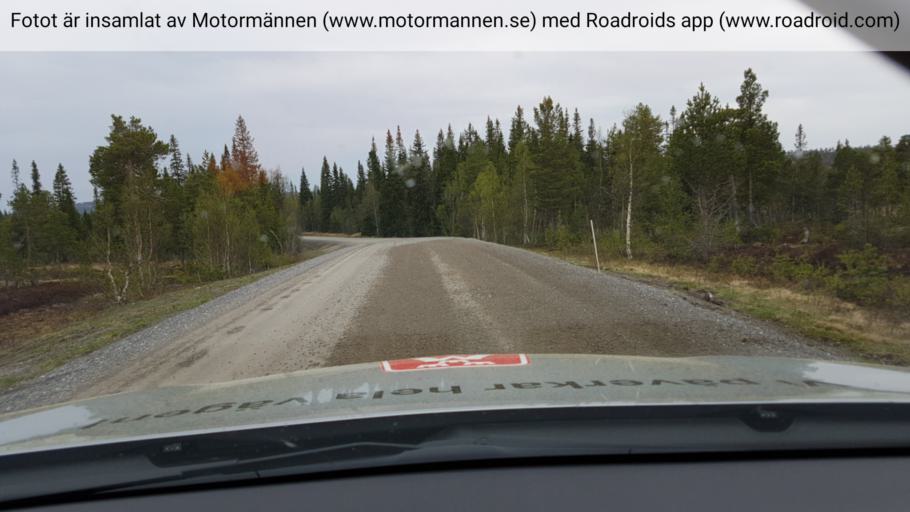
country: NO
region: Nord-Trondelag
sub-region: Snasa
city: Snaase
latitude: 63.7314
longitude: 12.4692
